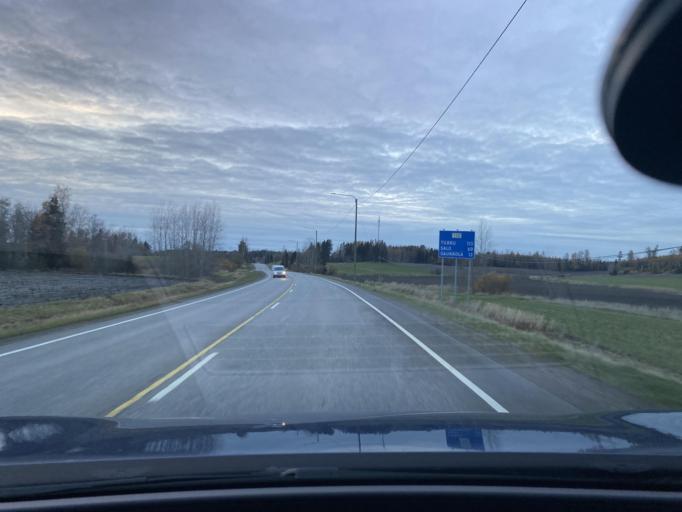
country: FI
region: Uusimaa
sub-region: Helsinki
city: Lohja
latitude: 60.3684
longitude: 24.1575
